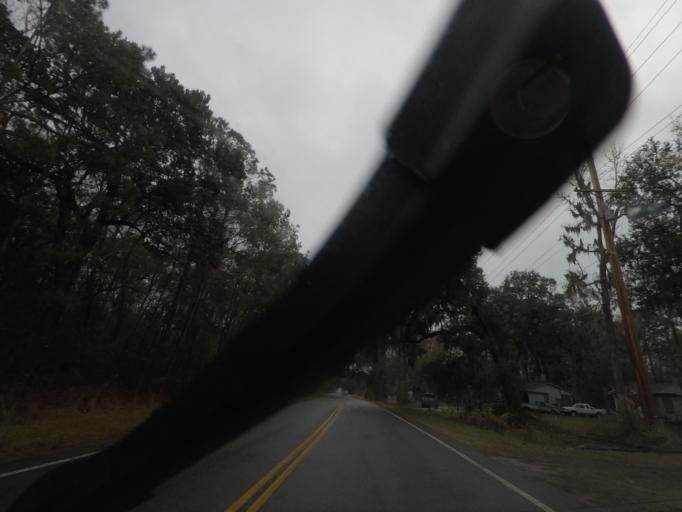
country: US
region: South Carolina
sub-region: Charleston County
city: Meggett
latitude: 32.6808
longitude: -80.3508
